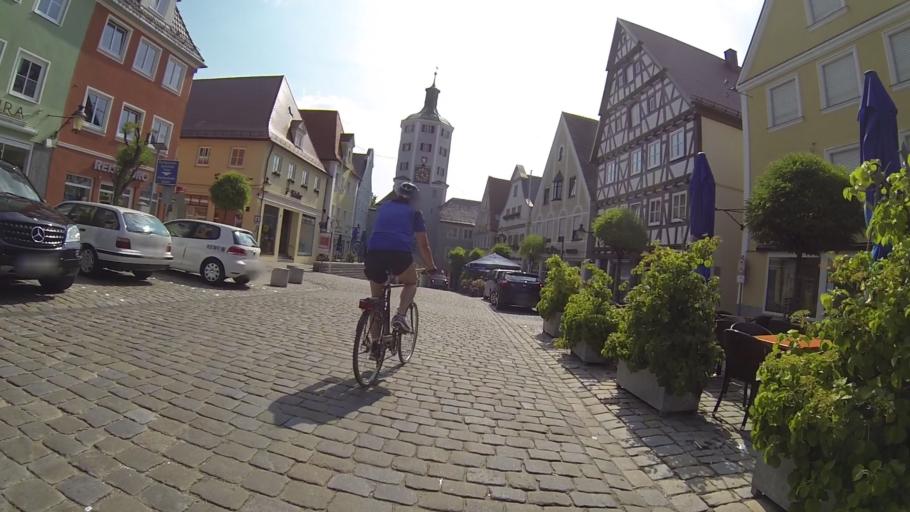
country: DE
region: Bavaria
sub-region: Swabia
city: Guenzburg
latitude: 48.4552
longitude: 10.2755
